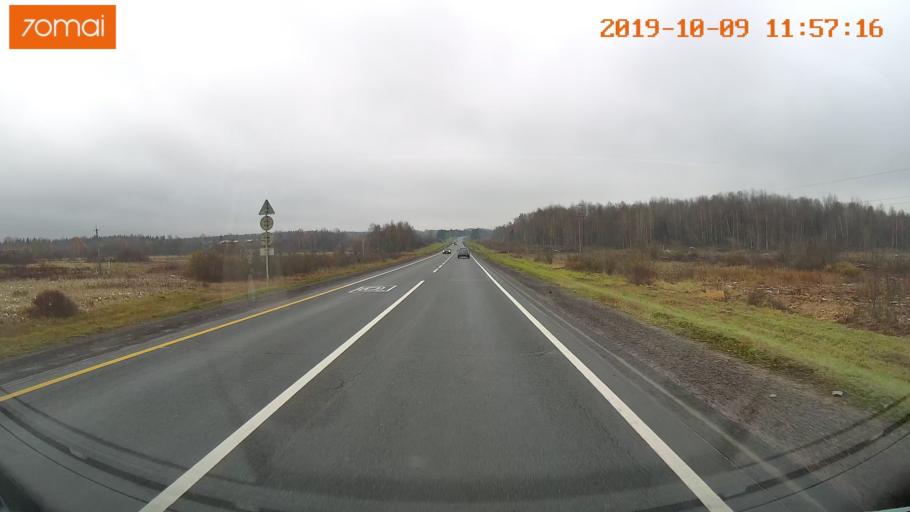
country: RU
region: Vologda
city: Gryazovets
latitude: 58.7346
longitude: 40.2916
